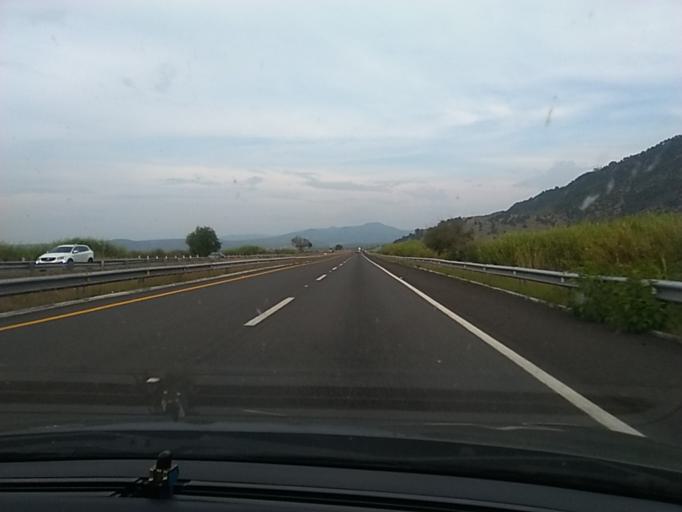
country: MX
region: Michoacan
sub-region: Zinapecuaro
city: Jose Maria Morelos (La Yegueeria)
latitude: 19.8986
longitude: -100.8854
